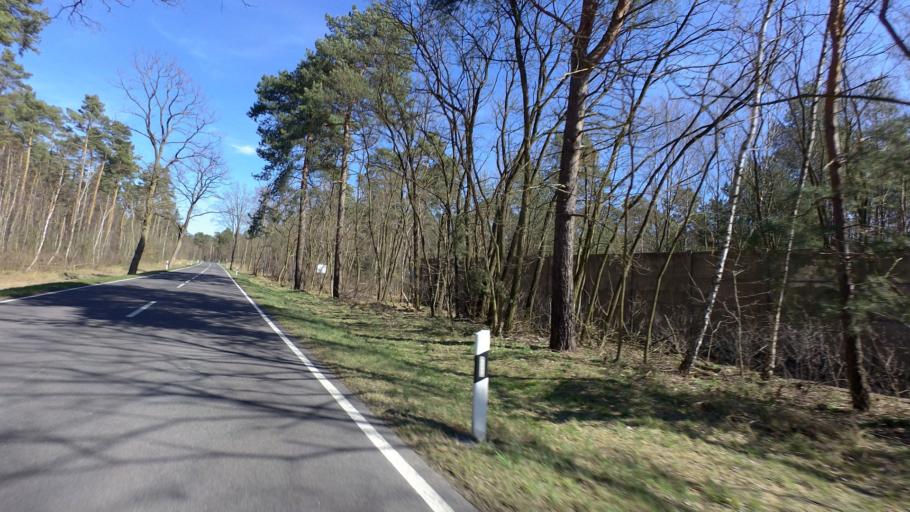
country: DE
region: Brandenburg
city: Storkow
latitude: 52.2129
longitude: 13.9402
